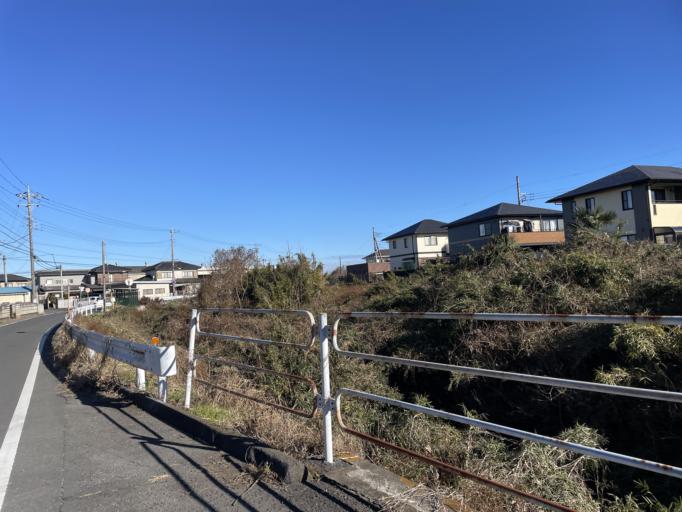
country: JP
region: Ibaraki
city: Yuki
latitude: 36.3107
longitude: 139.8757
